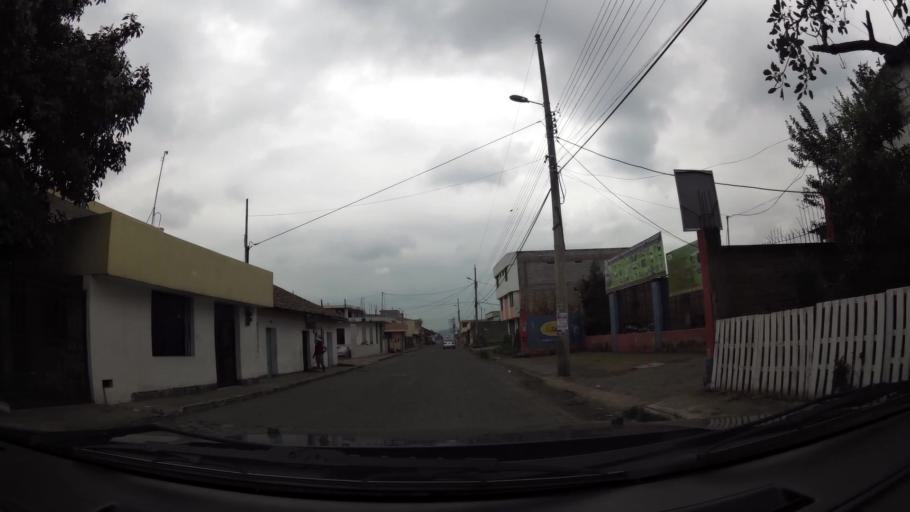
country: EC
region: Pichincha
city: Sangolqui
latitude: -0.3349
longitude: -78.4710
